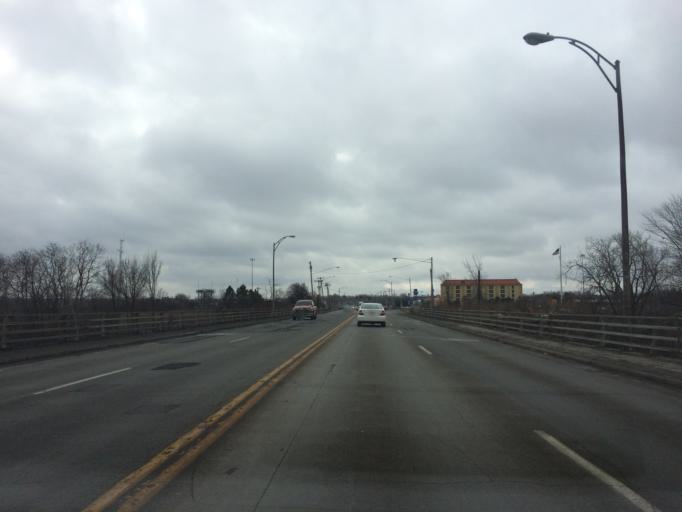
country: US
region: New York
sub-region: Monroe County
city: Rochester
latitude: 43.1110
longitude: -77.6161
